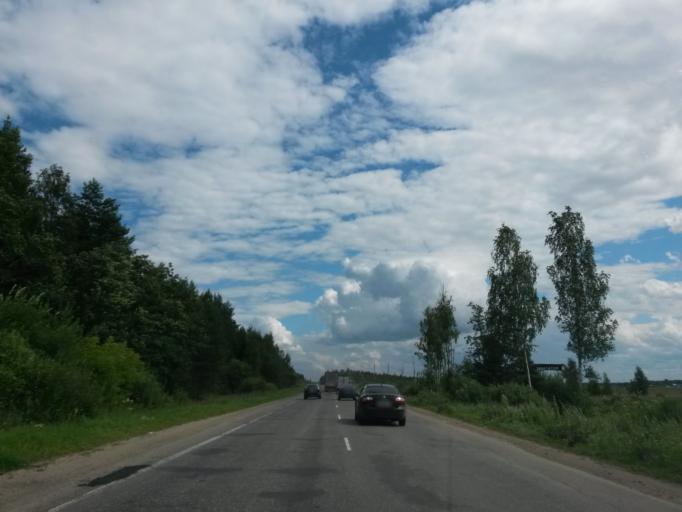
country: RU
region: Ivanovo
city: Novo-Talitsy
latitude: 57.0159
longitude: 40.7889
